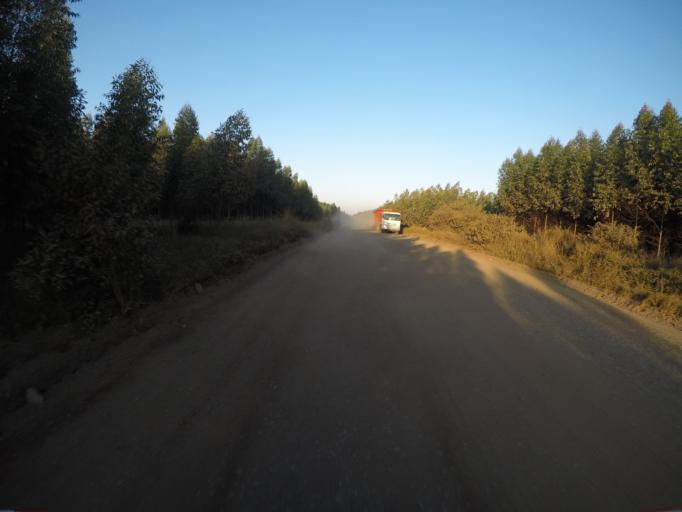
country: ZA
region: KwaZulu-Natal
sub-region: uThungulu District Municipality
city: KwaMbonambi
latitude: -28.6670
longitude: 32.0689
